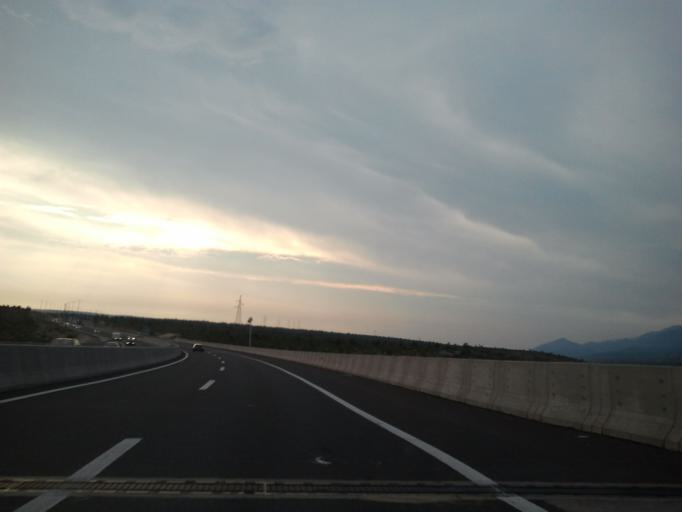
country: HR
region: Zadarska
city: Pridraga
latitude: 44.2412
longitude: 15.5824
